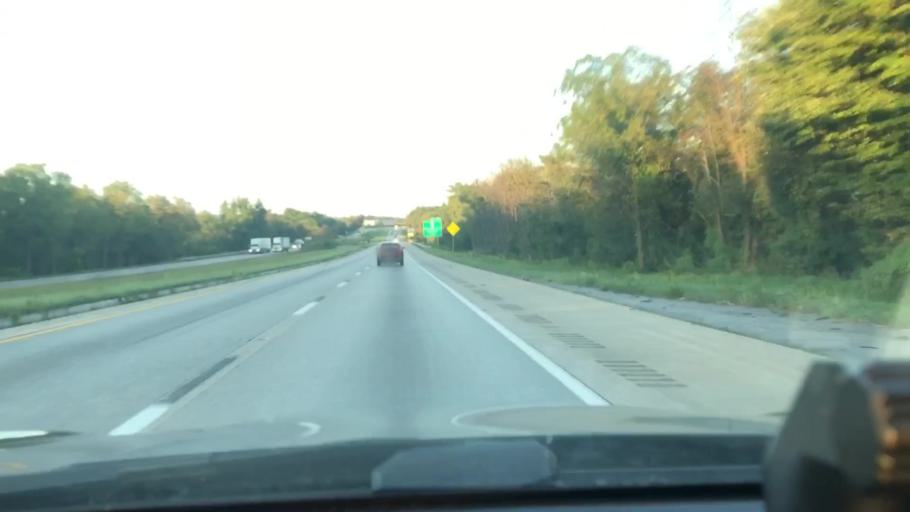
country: US
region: Pennsylvania
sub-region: Dauphin County
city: Skyline View
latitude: 40.3433
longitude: -76.7435
